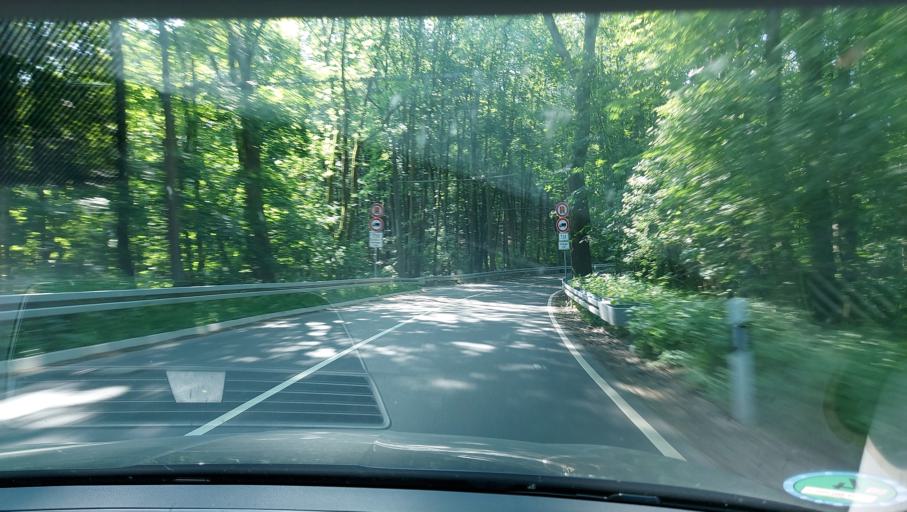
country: DE
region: North Rhine-Westphalia
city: Burscheid
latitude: 51.1422
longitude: 7.1323
